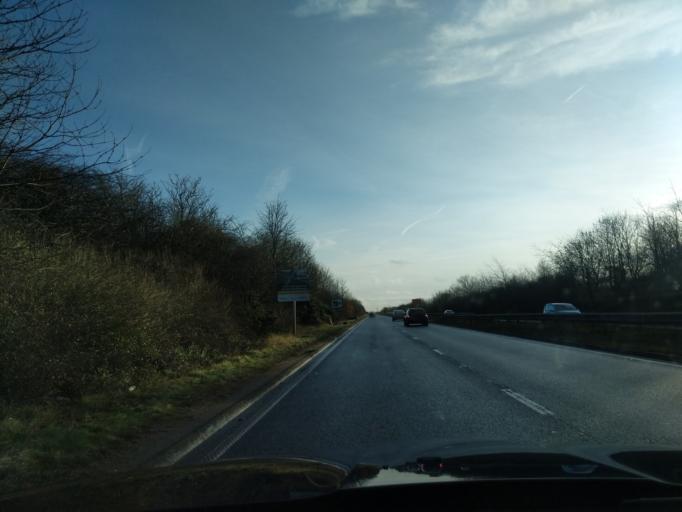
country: GB
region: England
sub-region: Borough of North Tyneside
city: Shiremoor
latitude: 55.0188
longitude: -1.5117
